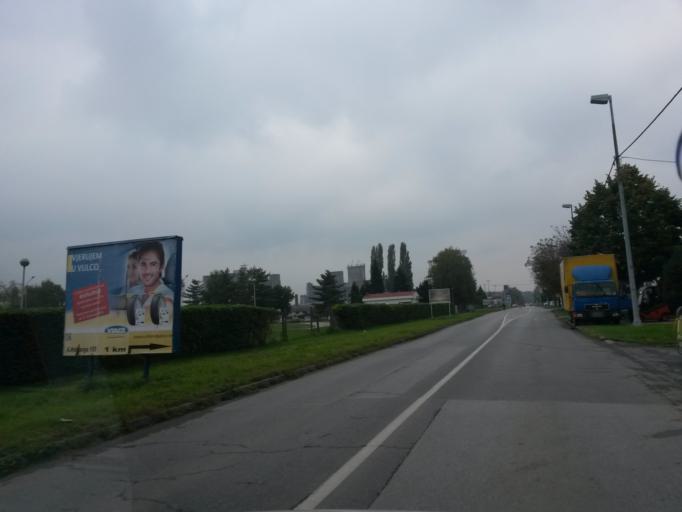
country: HR
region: Osjecko-Baranjska
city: Viskovci
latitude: 45.3252
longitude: 18.4177
